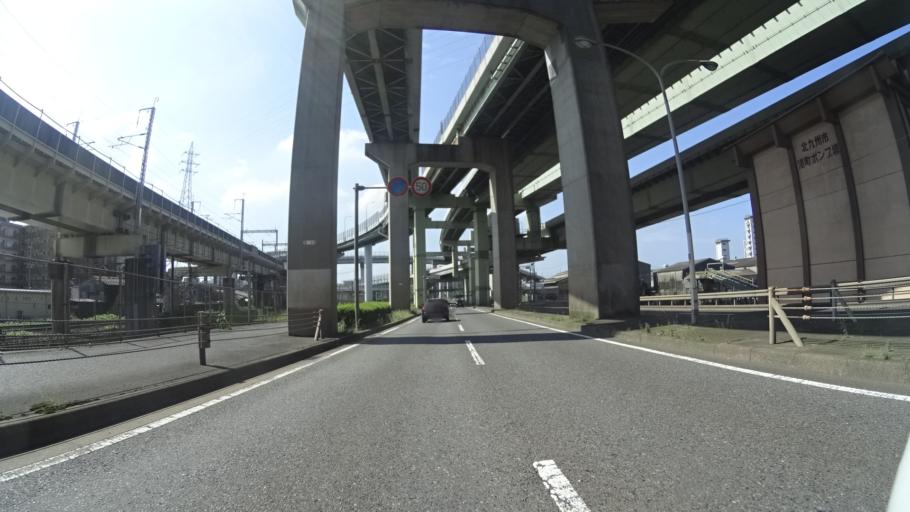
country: JP
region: Fukuoka
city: Kitakyushu
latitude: 33.8899
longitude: 130.8706
